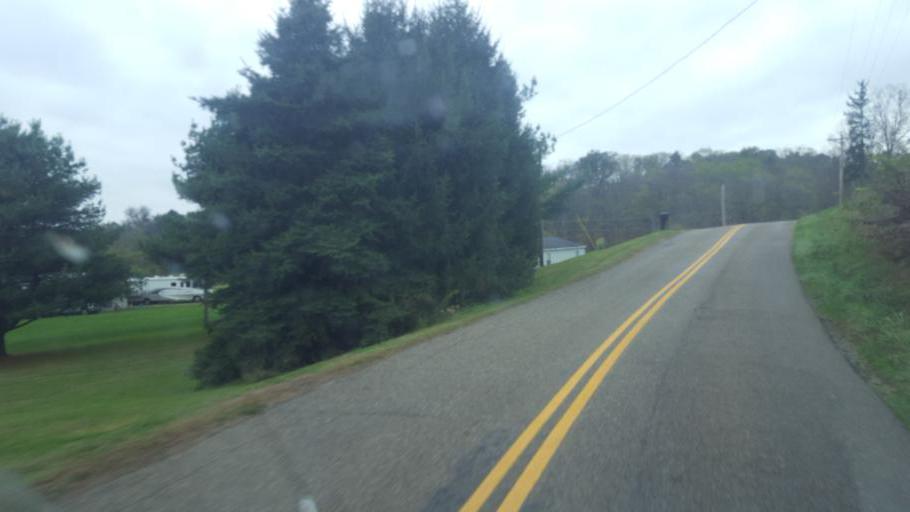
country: US
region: Ohio
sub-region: Carroll County
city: Carrollton
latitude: 40.4828
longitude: -81.0856
